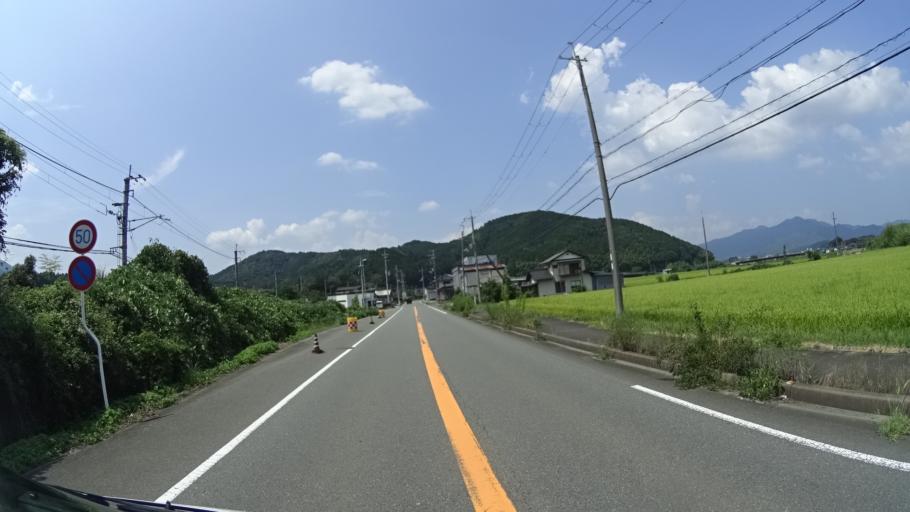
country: JP
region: Kyoto
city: Fukuchiyama
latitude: 35.2753
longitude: 135.1391
